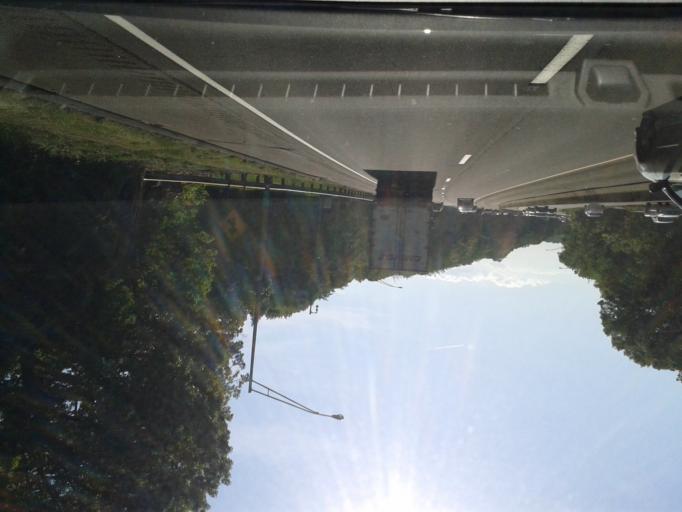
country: US
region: Connecticut
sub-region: New Haven County
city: Branford
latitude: 41.2947
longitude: -72.7869
